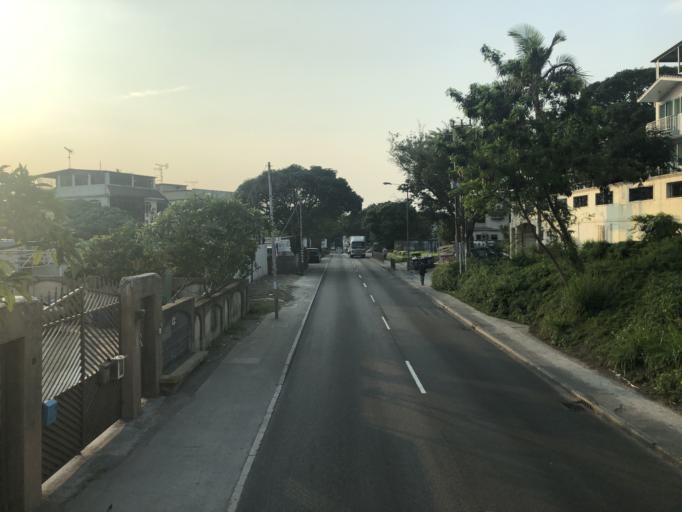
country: HK
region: Yuen Long
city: Yuen Long Kau Hui
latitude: 22.4632
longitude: 113.9874
